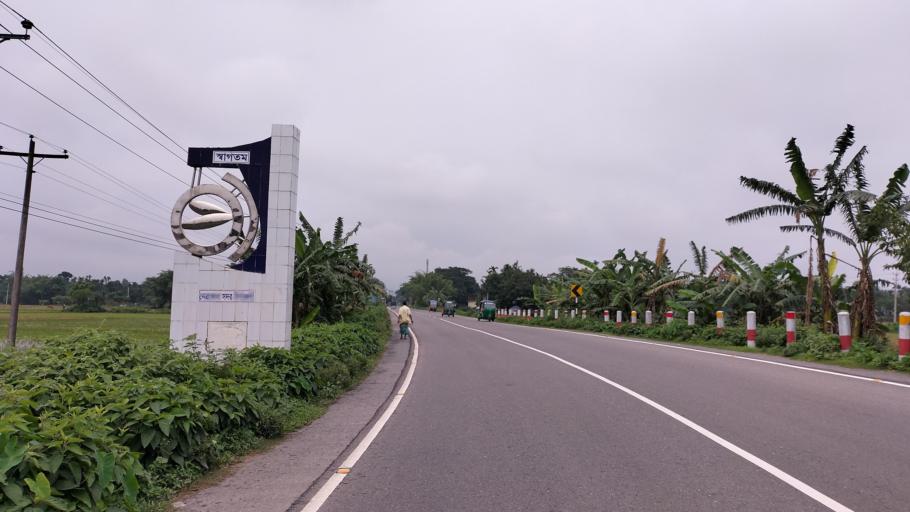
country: BD
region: Dhaka
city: Netrakona
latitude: 24.8524
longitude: 90.6553
